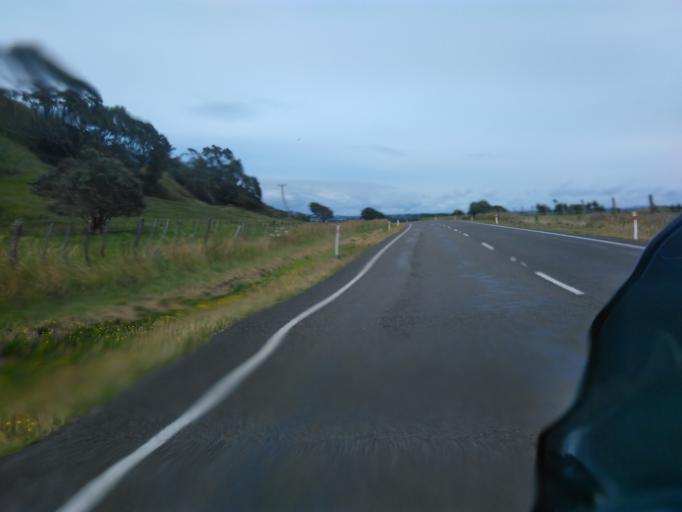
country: NZ
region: Bay of Plenty
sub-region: Opotiki District
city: Opotiki
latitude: -37.9915
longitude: 177.3068
